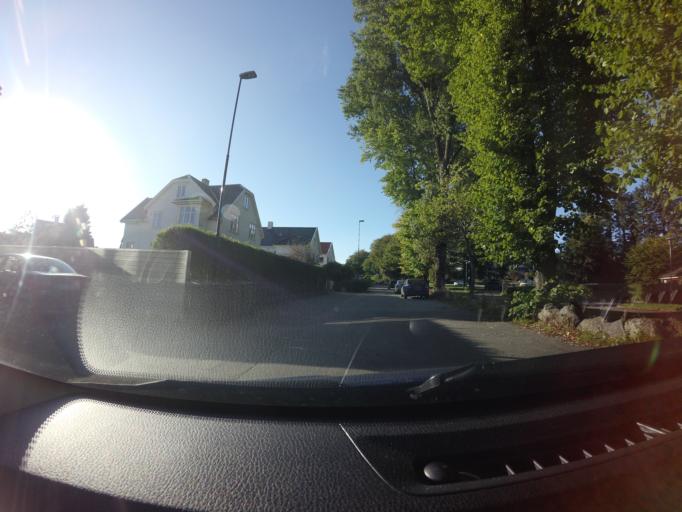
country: NO
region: Rogaland
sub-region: Stavanger
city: Stavanger
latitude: 58.9509
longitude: 5.7342
